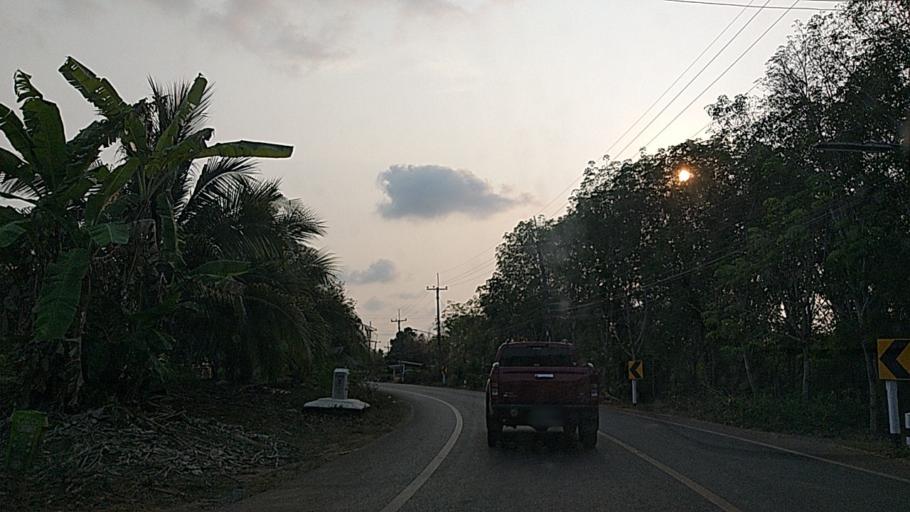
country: TH
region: Trat
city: Laem Ngop
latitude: 12.2157
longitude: 102.2985
